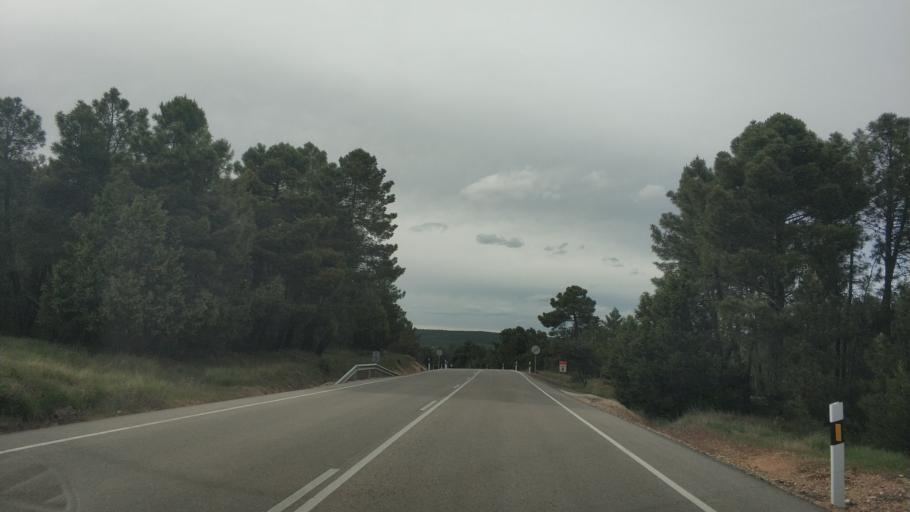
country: ES
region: Castille and Leon
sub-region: Provincia de Soria
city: Valdenebro
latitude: 41.5515
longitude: -2.9623
